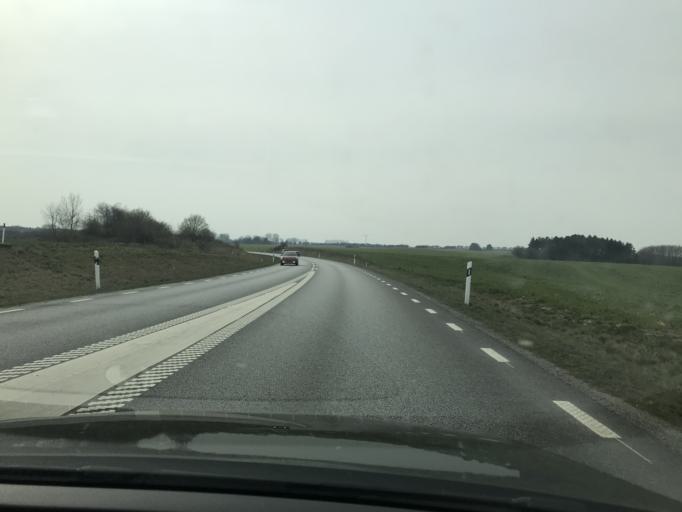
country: SE
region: Skane
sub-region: Ystads Kommun
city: Ystad
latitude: 55.4353
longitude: 13.7816
